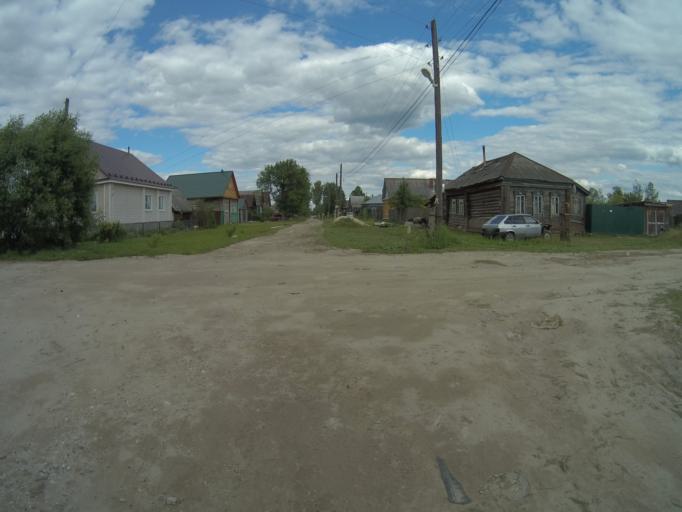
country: RU
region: Vladimir
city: Sudogda
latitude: 55.9551
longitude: 40.8532
